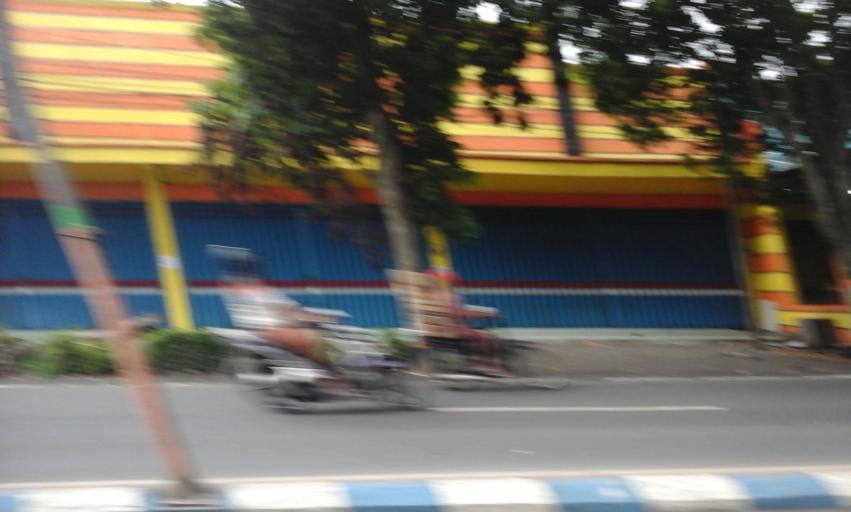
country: ID
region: East Java
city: Sukodono
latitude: -8.0987
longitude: 113.2341
